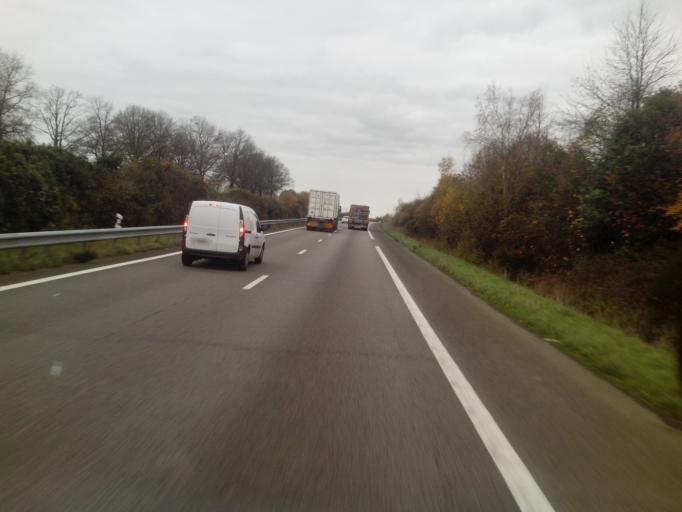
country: FR
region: Pays de la Loire
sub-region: Departement de la Loire-Atlantique
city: La Grigonnais
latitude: 47.5286
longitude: -1.6385
